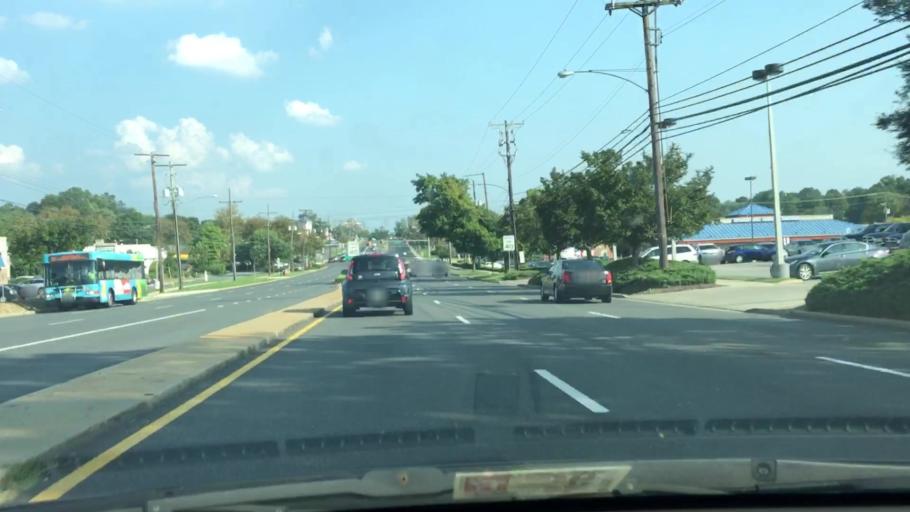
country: US
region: Maryland
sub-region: Montgomery County
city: Rockville
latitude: 39.0787
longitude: -77.1418
